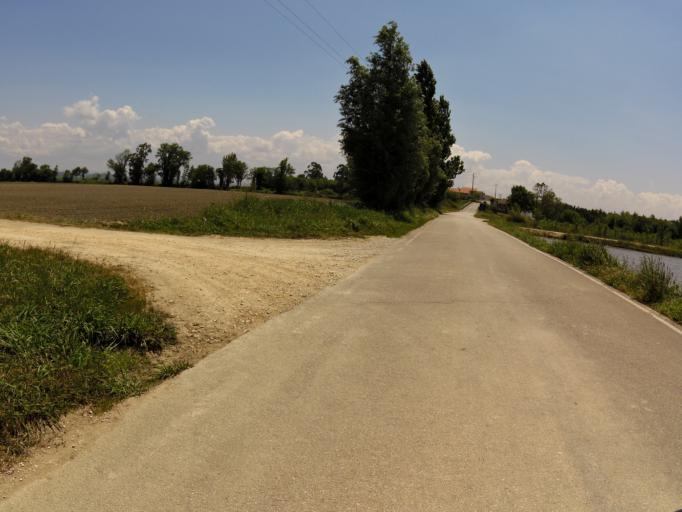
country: PT
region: Coimbra
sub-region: Montemor-O-Velho
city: Montemor-o-Velho
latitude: 40.1619
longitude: -8.7157
